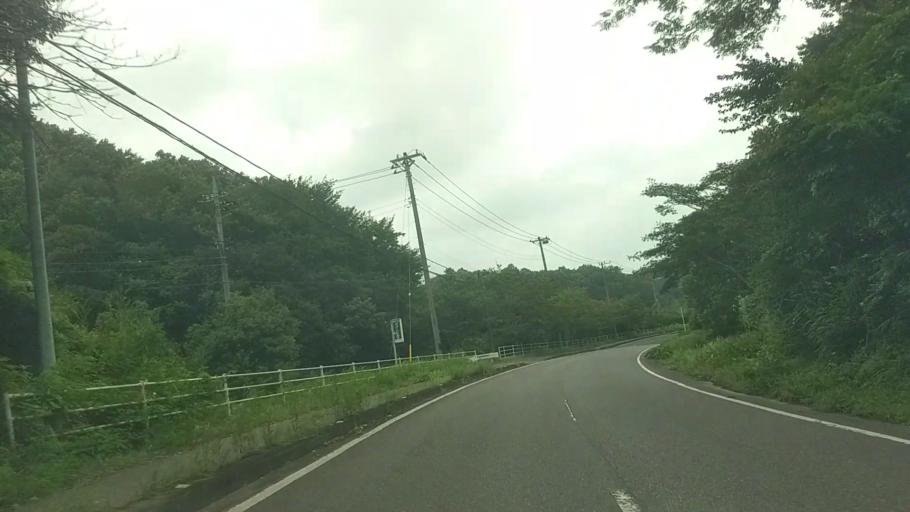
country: JP
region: Chiba
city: Kawaguchi
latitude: 35.2426
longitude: 140.0355
